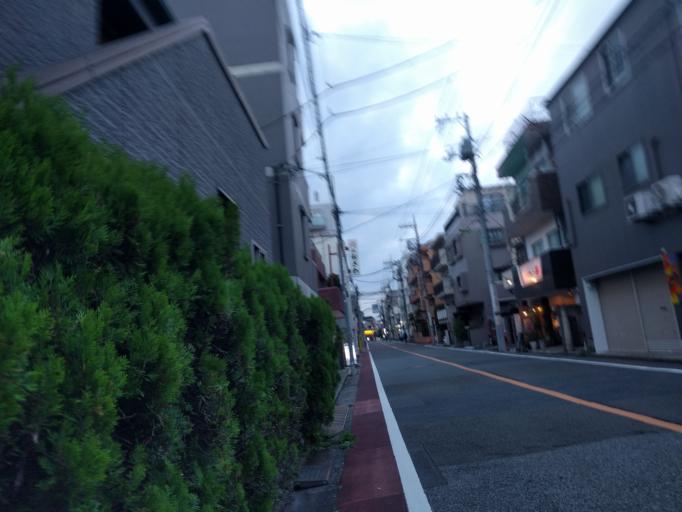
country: JP
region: Tokyo
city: Tokyo
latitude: 35.6486
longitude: 139.6382
